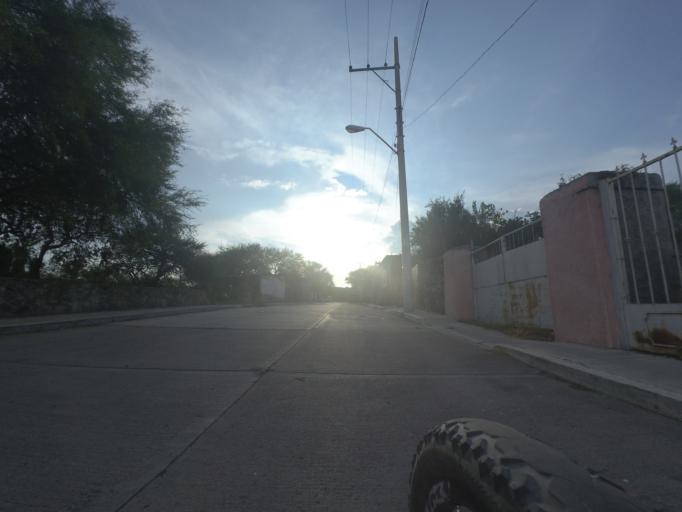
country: MX
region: Aguascalientes
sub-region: Aguascalientes
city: Los Canos
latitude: 21.7804
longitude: -102.3758
